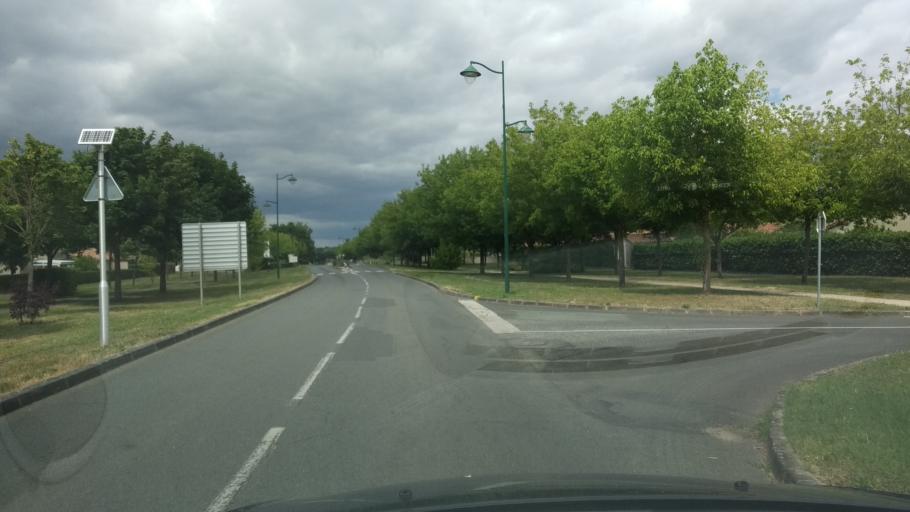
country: FR
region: Poitou-Charentes
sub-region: Departement de la Vienne
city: Vouneuil-sous-Biard
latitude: 46.5693
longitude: 0.2729
